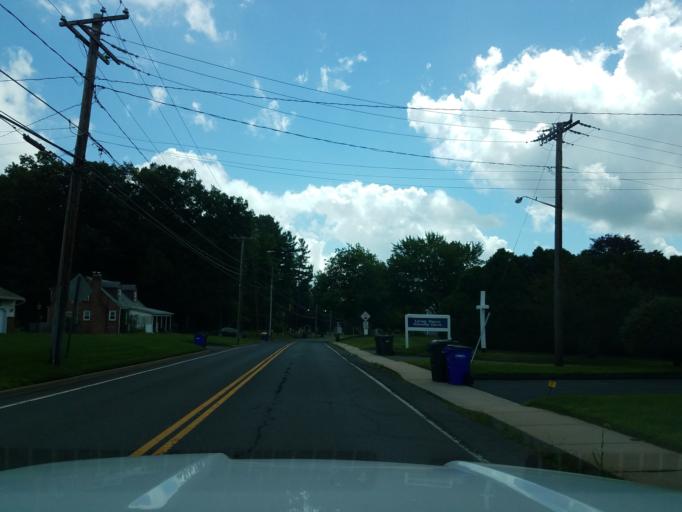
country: US
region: Connecticut
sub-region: Hartford County
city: Windsor Locks
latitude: 41.9312
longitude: -72.6485
